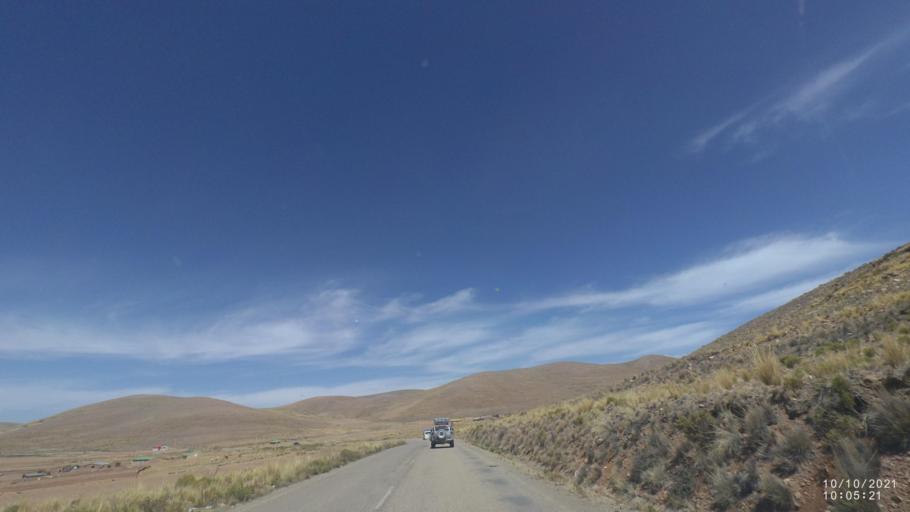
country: BO
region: La Paz
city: Eucaliptus
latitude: -17.3769
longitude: -67.4554
